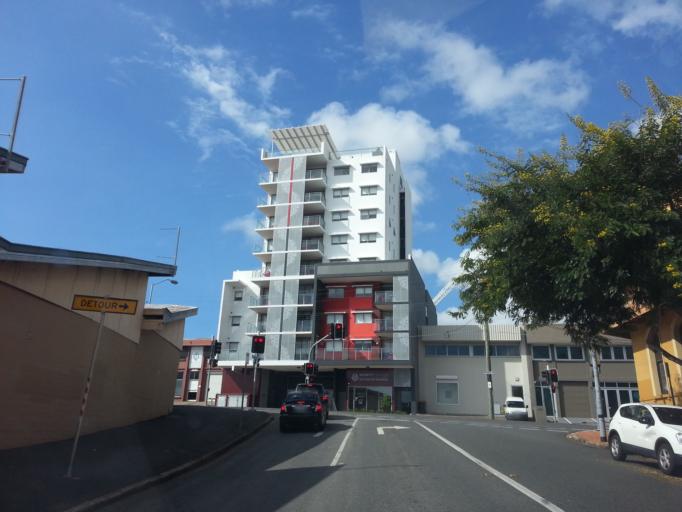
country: AU
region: Queensland
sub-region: Brisbane
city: Fortitude Valley
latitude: -27.4500
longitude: 153.0349
